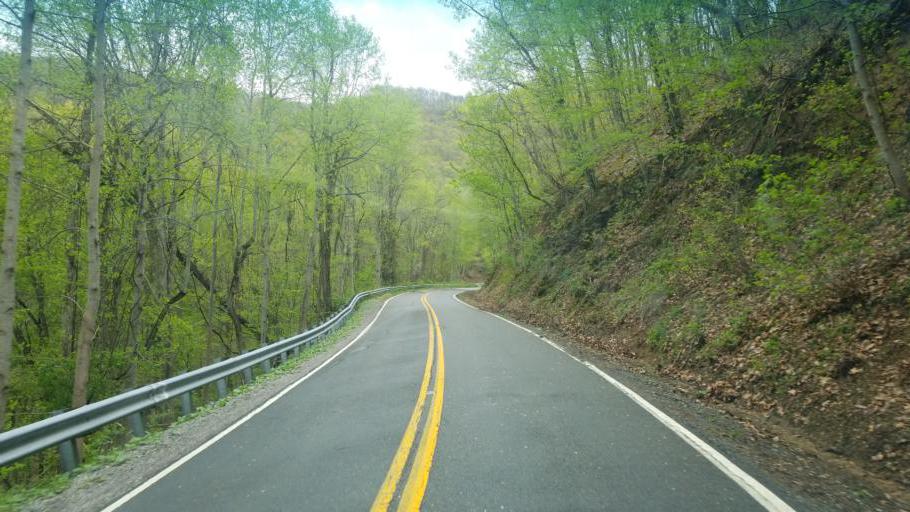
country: US
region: Virginia
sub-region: Tazewell County
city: Tazewell
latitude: 37.0086
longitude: -81.5174
